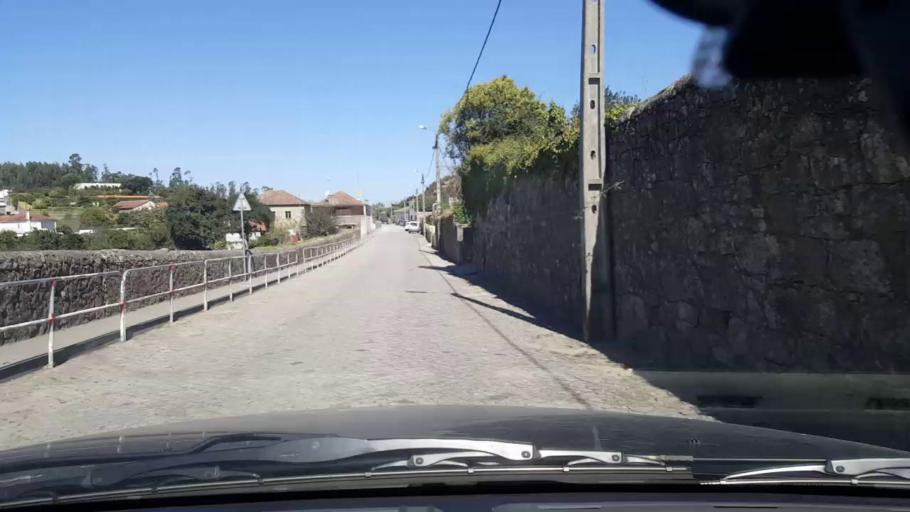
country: PT
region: Porto
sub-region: Maia
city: Gemunde
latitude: 41.3332
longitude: -8.6455
